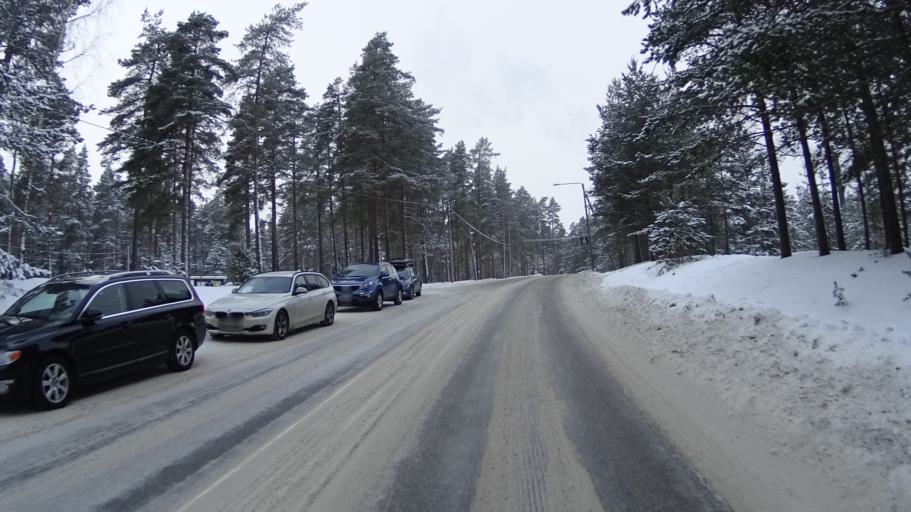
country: FI
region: Uusimaa
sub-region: Helsinki
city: Vihti
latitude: 60.3378
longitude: 24.3115
